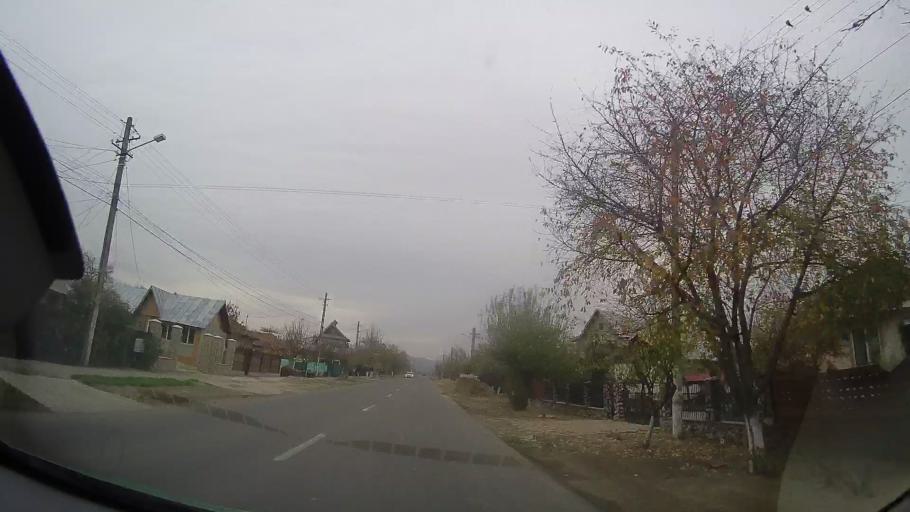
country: RO
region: Prahova
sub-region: Comuna Albesti-Paleologu
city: Albesti-Paleologu
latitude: 44.9611
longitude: 26.2330
